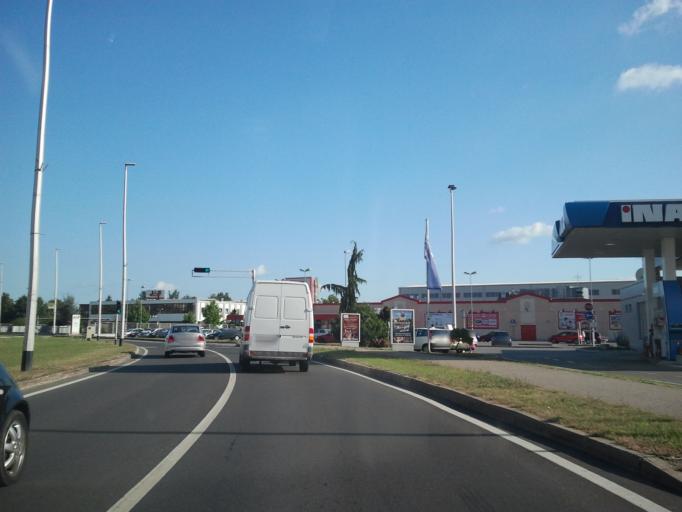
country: HR
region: Zagrebacka
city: Gradici
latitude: 45.7196
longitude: 16.0545
